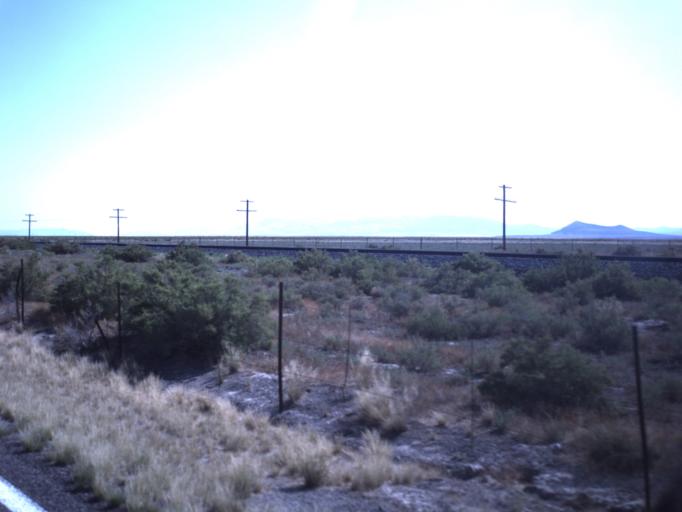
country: US
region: Utah
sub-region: Millard County
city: Delta
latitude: 39.0709
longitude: -112.7593
